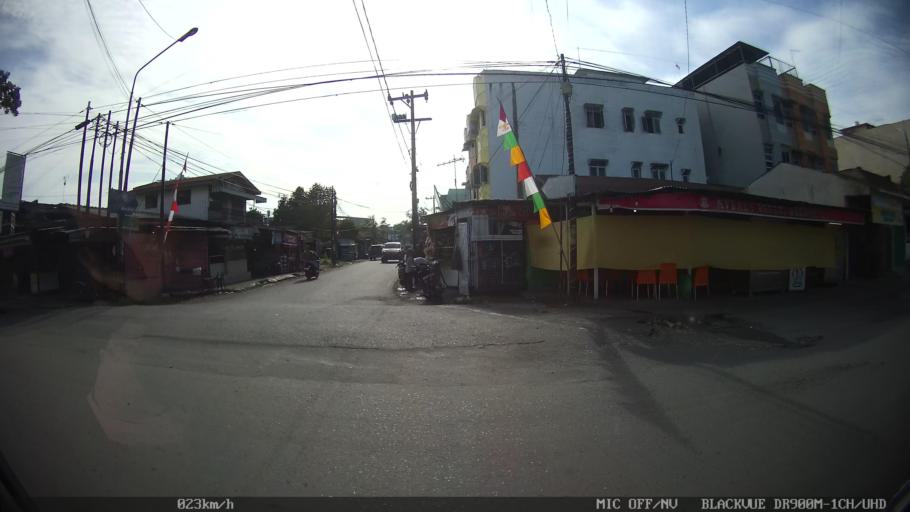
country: ID
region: North Sumatra
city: Medan
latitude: 3.6034
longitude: 98.6650
